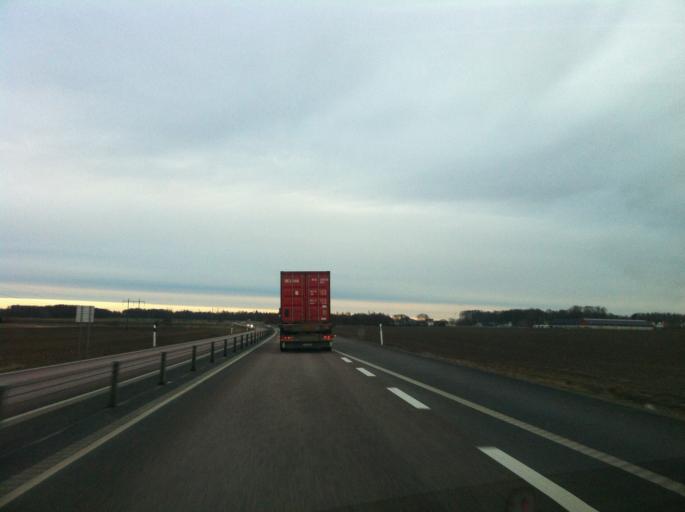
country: SE
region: Skane
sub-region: Helsingborg
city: Helsingborg
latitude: 56.0940
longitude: 12.6851
